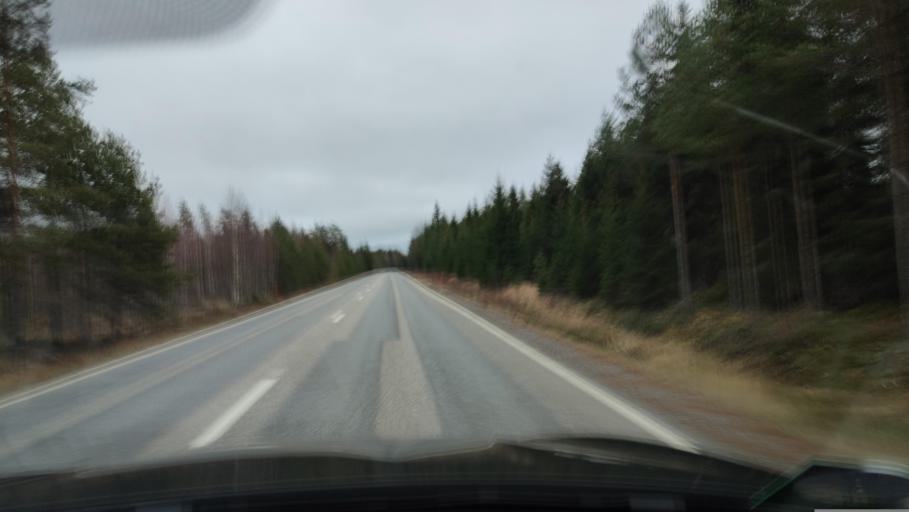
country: FI
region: Southern Ostrobothnia
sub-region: Suupohja
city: Karijoki
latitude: 62.2324
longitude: 21.7206
